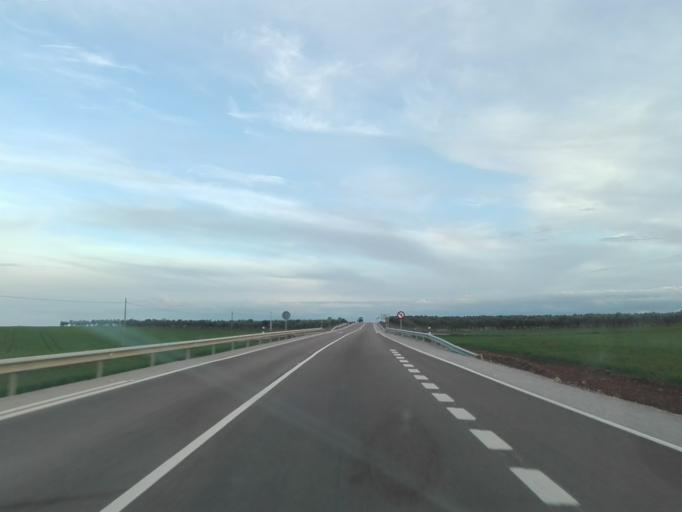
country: ES
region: Extremadura
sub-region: Provincia de Badajoz
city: Usagre
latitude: 38.3434
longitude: -6.1678
